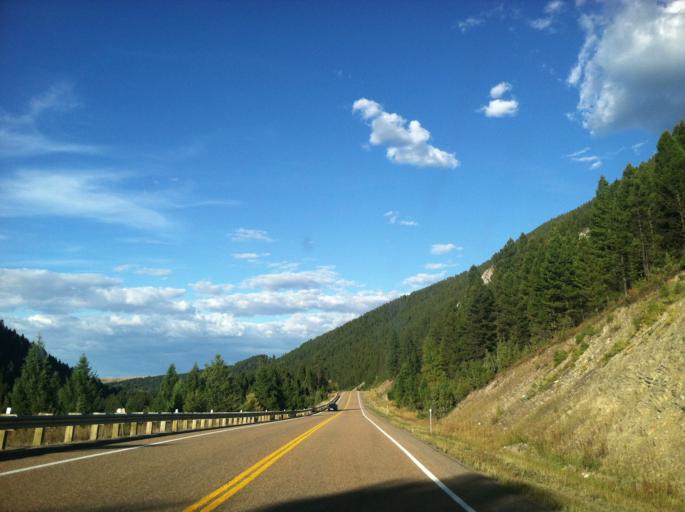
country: US
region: Montana
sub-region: Granite County
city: Philipsburg
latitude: 46.4484
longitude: -113.2488
